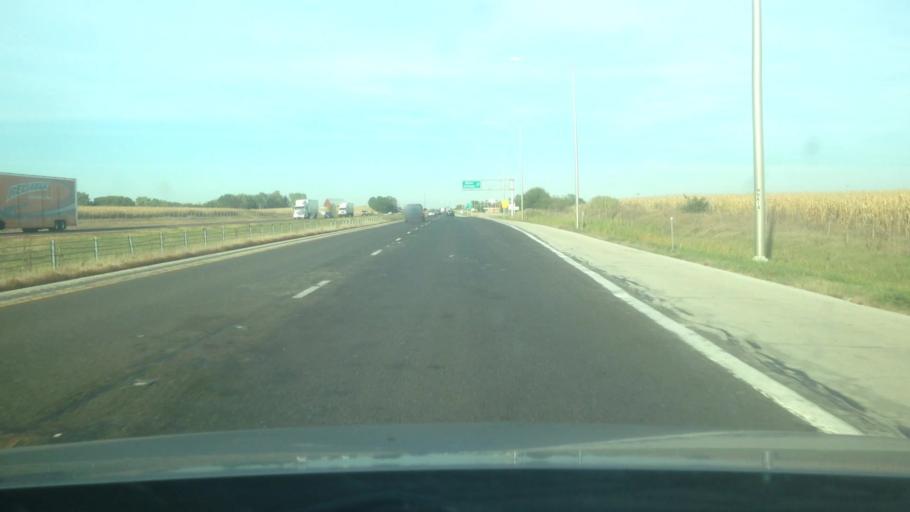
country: US
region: Illinois
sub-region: Will County
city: Peotone
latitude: 41.3566
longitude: -87.8094
